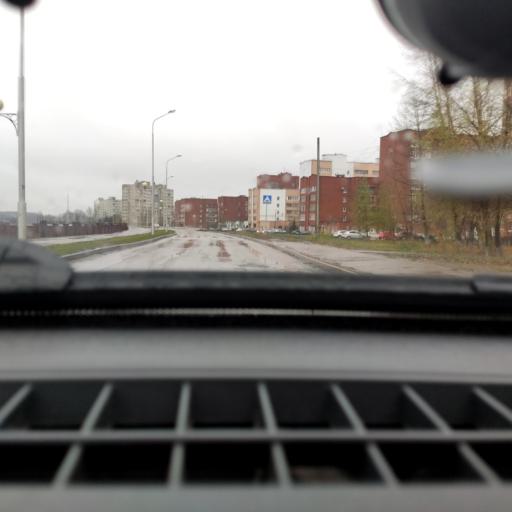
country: RU
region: Bashkortostan
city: Ufa
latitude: 54.7795
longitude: 56.0784
